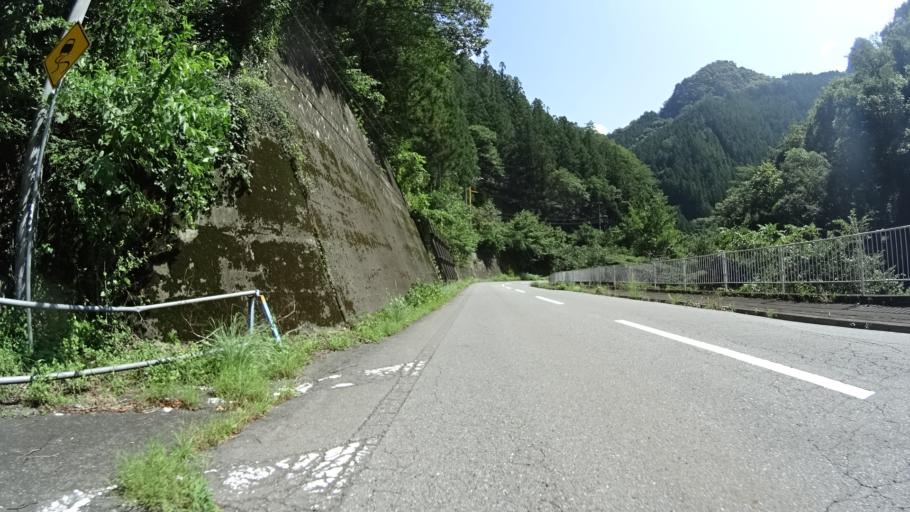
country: JP
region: Gunma
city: Tomioka
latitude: 36.0845
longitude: 138.8254
